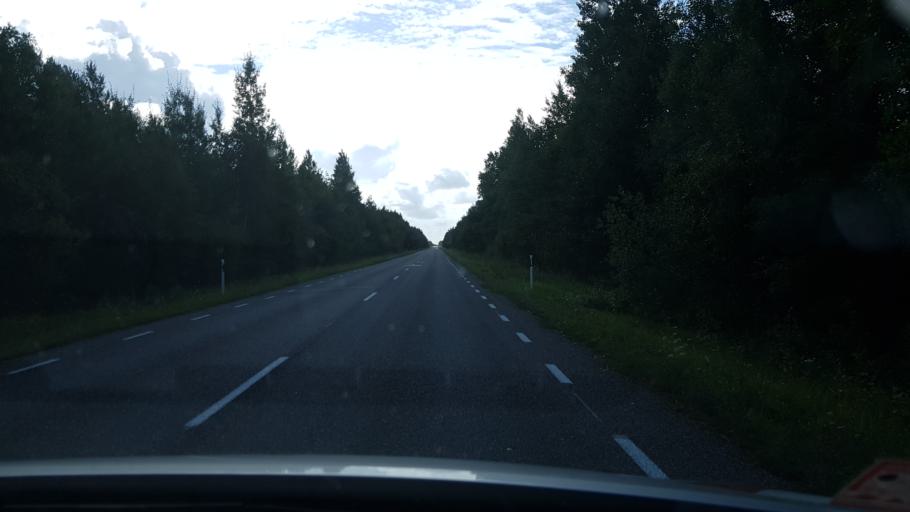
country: EE
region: Saare
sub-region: Kuressaare linn
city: Kuressaare
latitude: 58.4371
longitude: 21.9917
